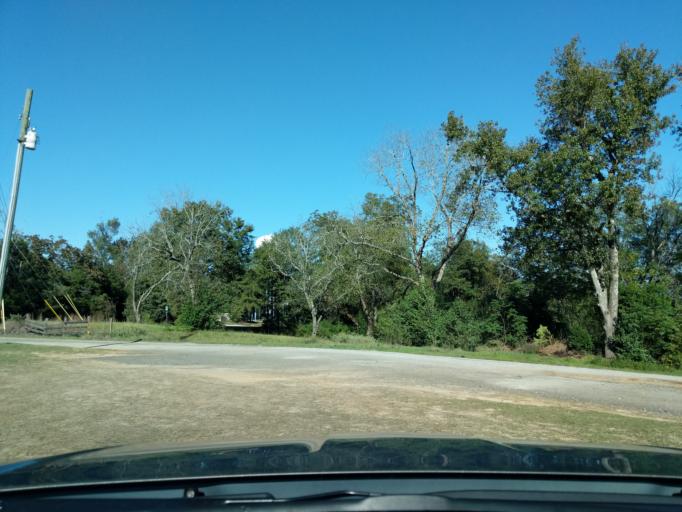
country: US
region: Georgia
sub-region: Columbia County
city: Grovetown
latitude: 33.4695
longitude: -82.1546
